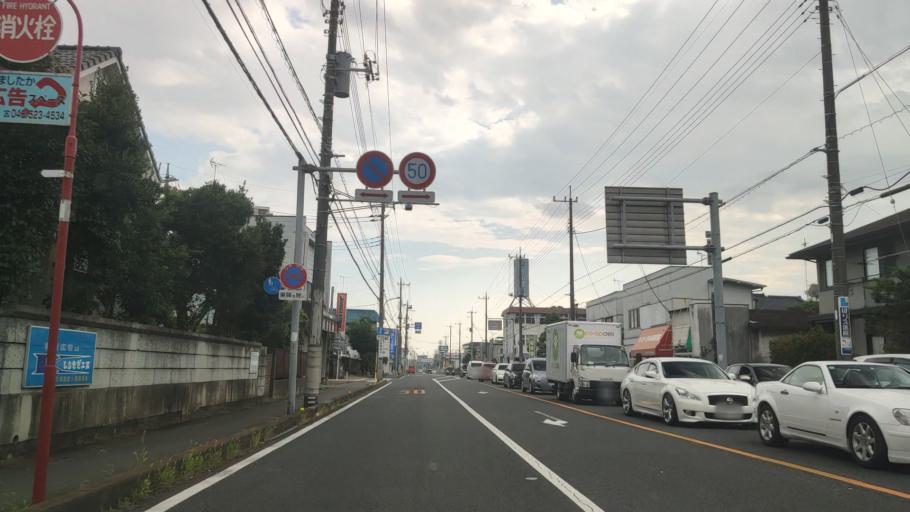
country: JP
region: Tochigi
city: Utsunomiya-shi
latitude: 36.5738
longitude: 139.9043
